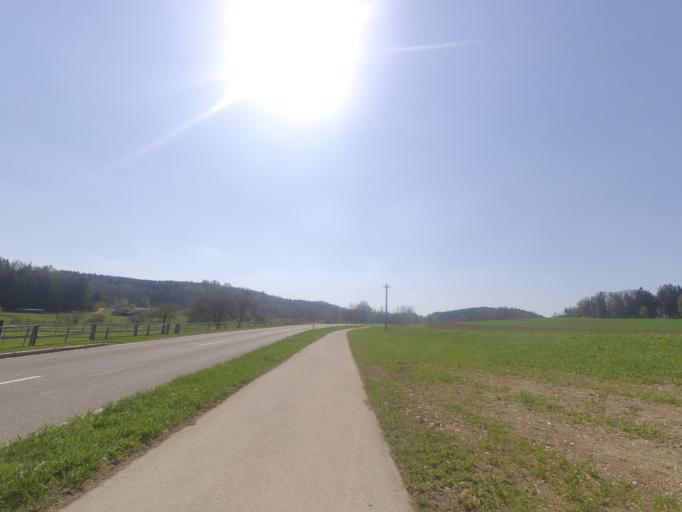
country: DE
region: Bavaria
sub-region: Swabia
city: Pfaffenhofen an der Roth
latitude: 48.3299
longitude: 10.2094
